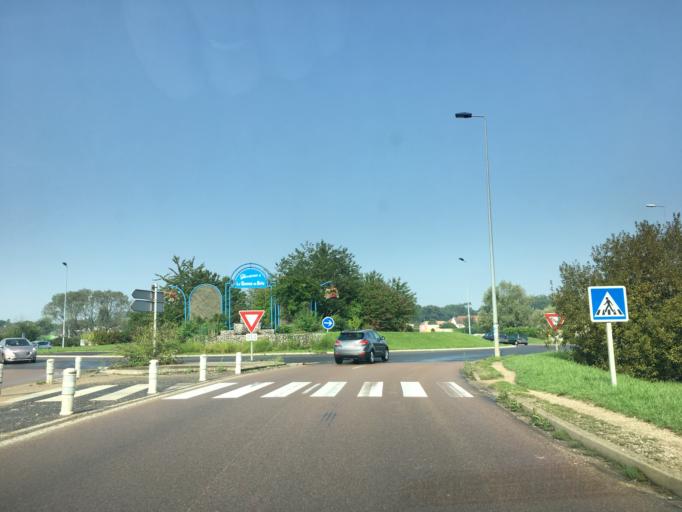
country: FR
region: Ile-de-France
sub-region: Departement du Val-de-Marne
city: La Queue-en-Brie
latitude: 48.7786
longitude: 2.5869
